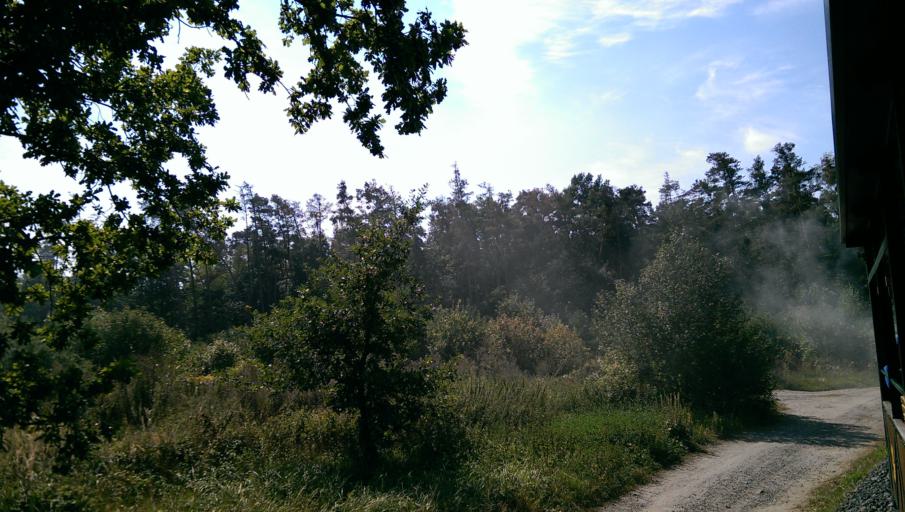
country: CZ
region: Central Bohemia
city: Stary Kolin
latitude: 50.0550
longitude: 15.2651
